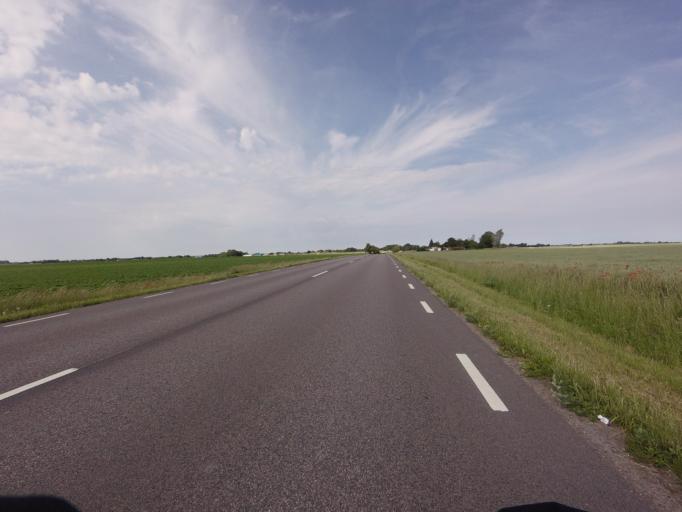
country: SE
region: Skane
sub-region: Vellinge Kommun
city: Vellinge
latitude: 55.4994
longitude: 13.0262
